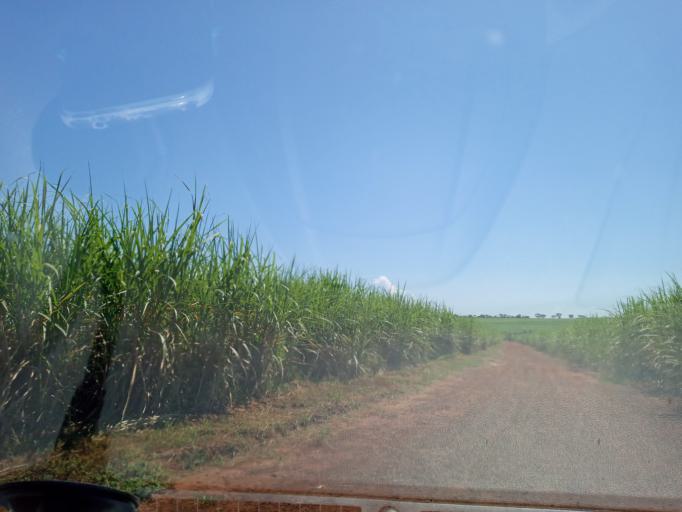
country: BR
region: Goias
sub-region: Itumbiara
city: Itumbiara
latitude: -18.4336
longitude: -49.1523
